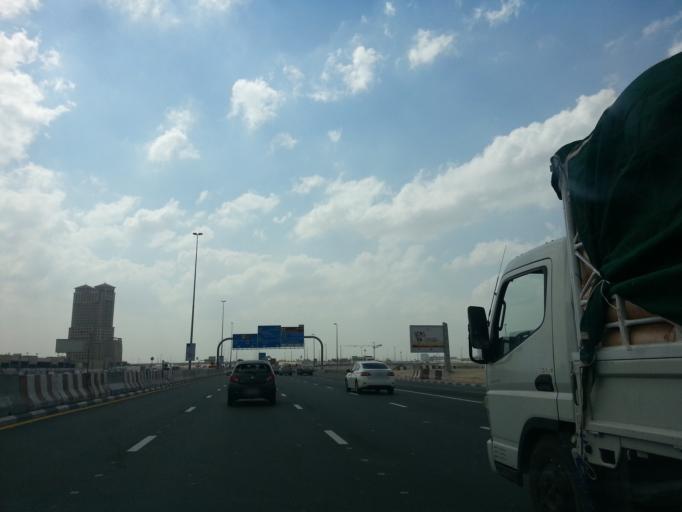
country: AE
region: Ash Shariqah
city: Sharjah
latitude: 25.2193
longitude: 55.3147
